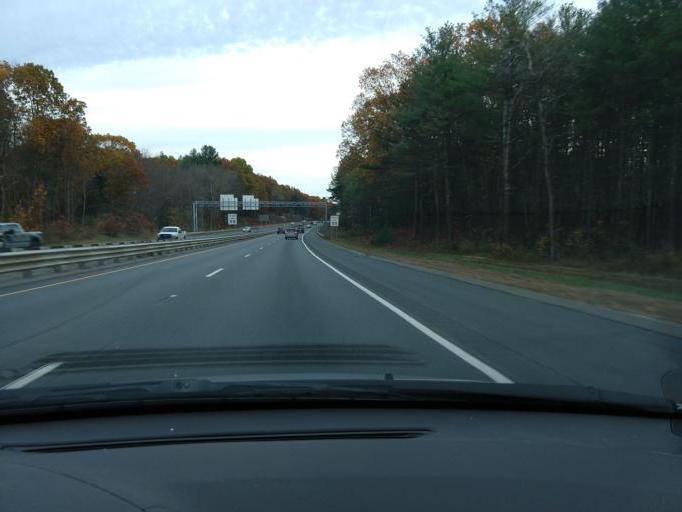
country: US
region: Massachusetts
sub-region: Middlesex County
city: Littleton Common
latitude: 42.5163
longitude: -71.4987
